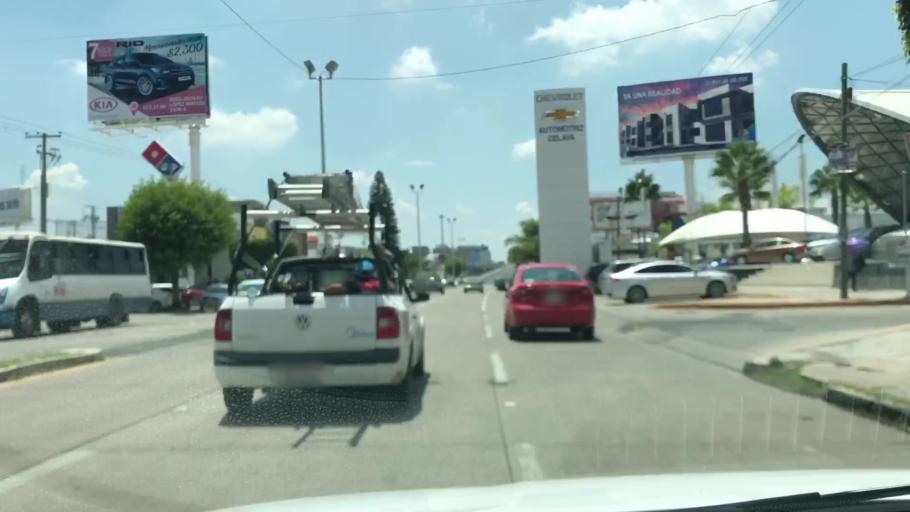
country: MX
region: Guanajuato
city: Celaya
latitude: 20.5190
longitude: -100.8353
